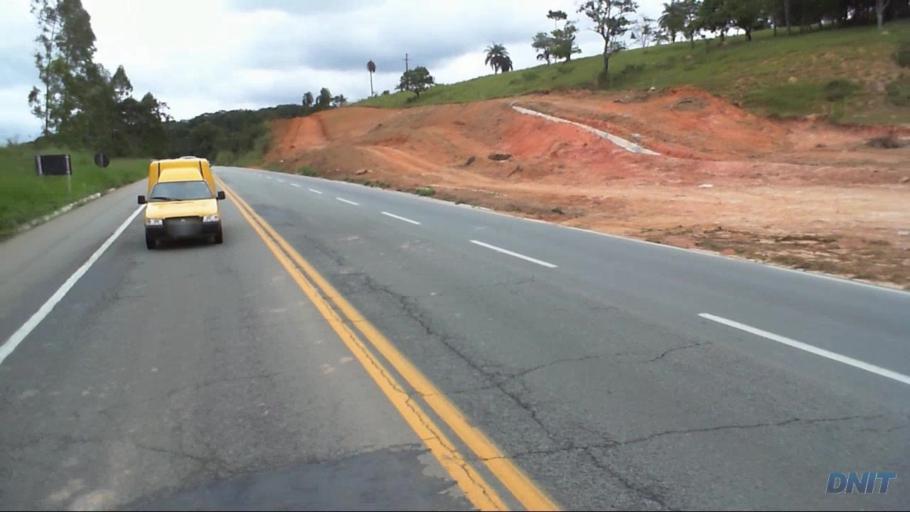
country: BR
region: Minas Gerais
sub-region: Barao De Cocais
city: Barao de Cocais
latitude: -19.7947
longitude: -43.4262
